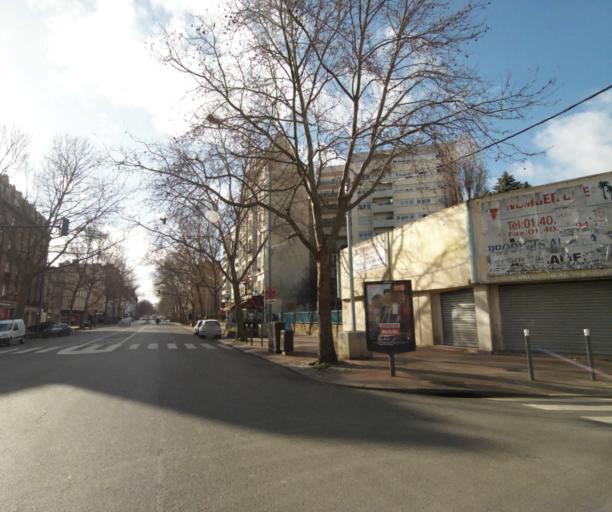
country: FR
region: Ile-de-France
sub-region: Paris
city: Saint-Ouen
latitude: 48.9074
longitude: 2.3441
